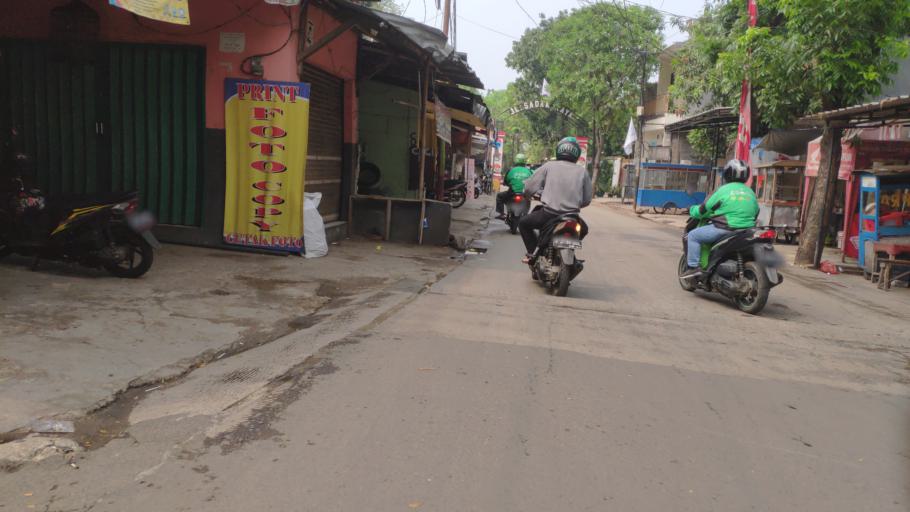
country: ID
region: West Java
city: Depok
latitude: -6.3441
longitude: 106.8123
